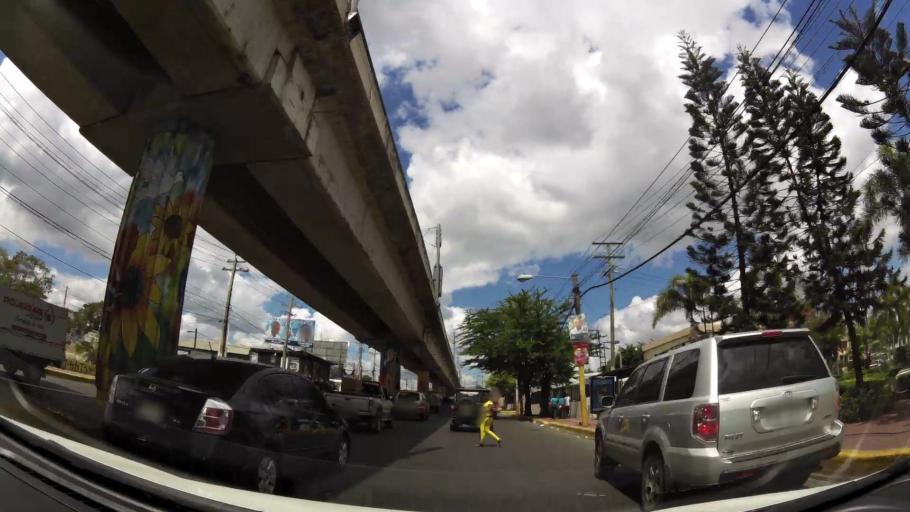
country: DO
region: Nacional
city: Ensanche Luperon
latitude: 18.5201
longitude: -69.9154
